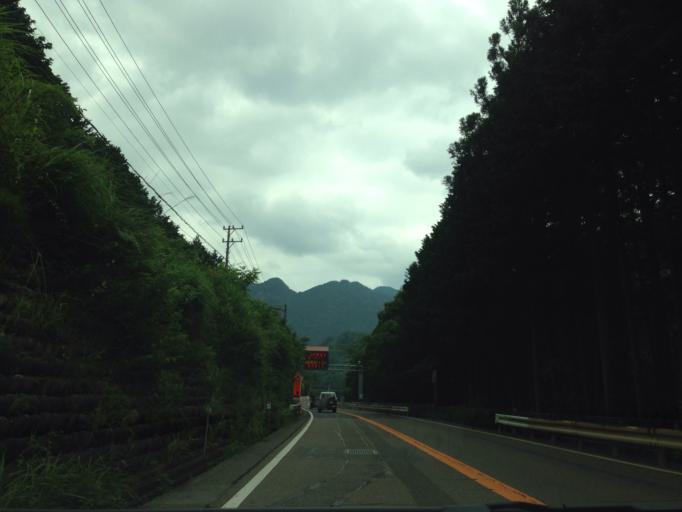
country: JP
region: Gifu
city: Mitake
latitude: 35.5906
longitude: 137.1704
